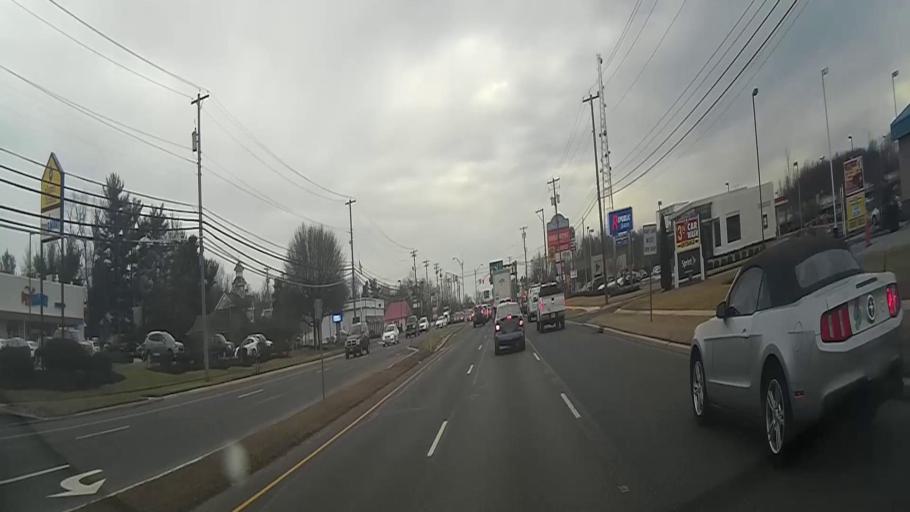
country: US
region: New Jersey
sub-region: Camden County
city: Berlin
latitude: 39.8072
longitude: -74.9314
